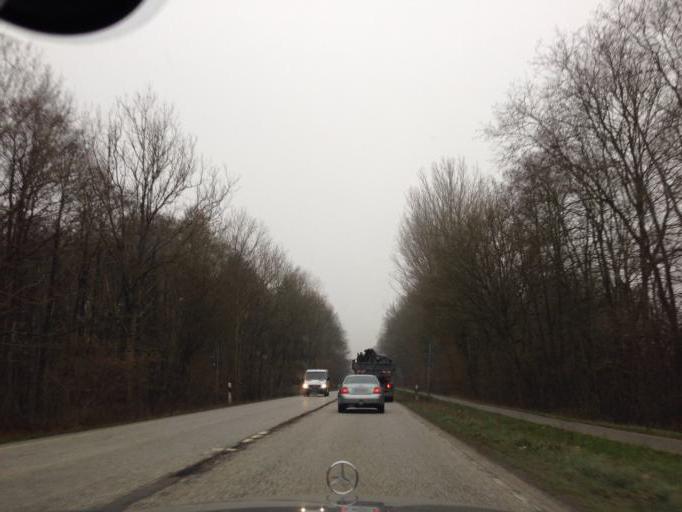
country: DE
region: Schleswig-Holstein
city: Klein Barkau
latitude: 54.2430
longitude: 10.1484
